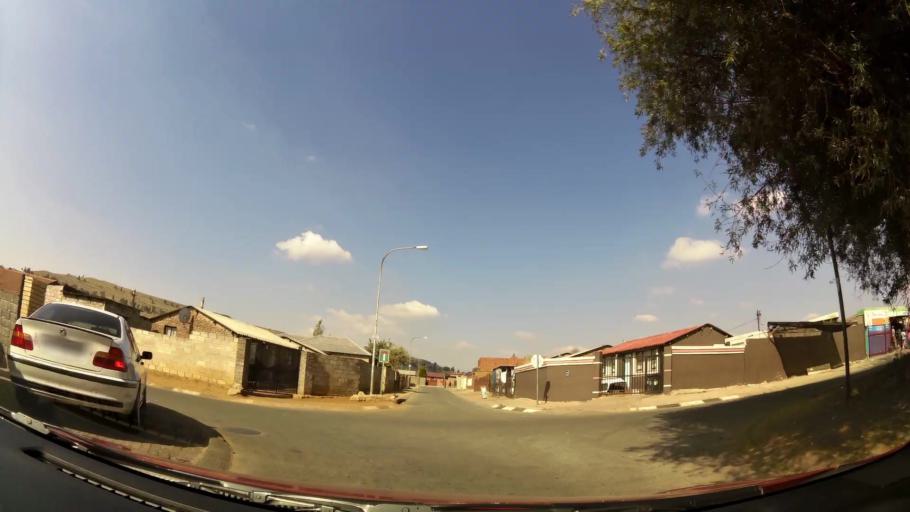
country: ZA
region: Gauteng
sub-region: City of Johannesburg Metropolitan Municipality
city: Johannesburg
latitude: -26.2360
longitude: 27.9552
